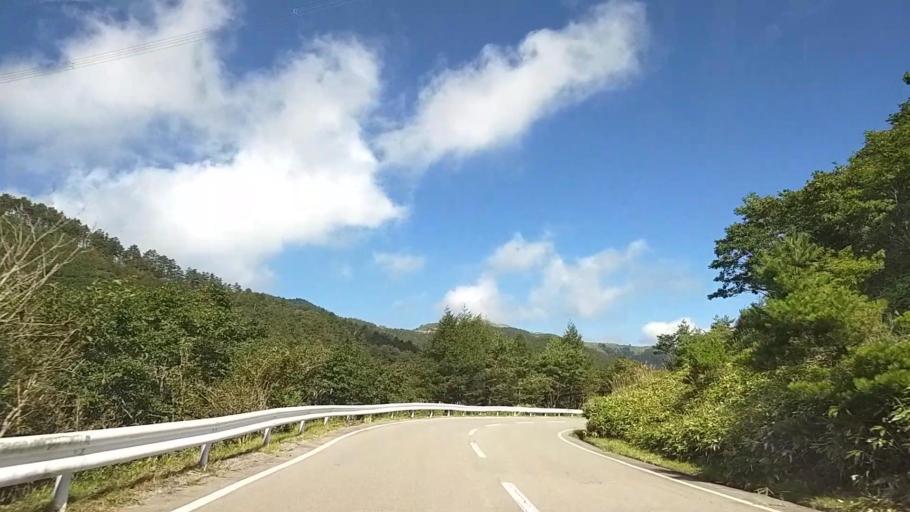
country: JP
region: Nagano
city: Suwa
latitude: 36.1425
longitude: 138.1450
